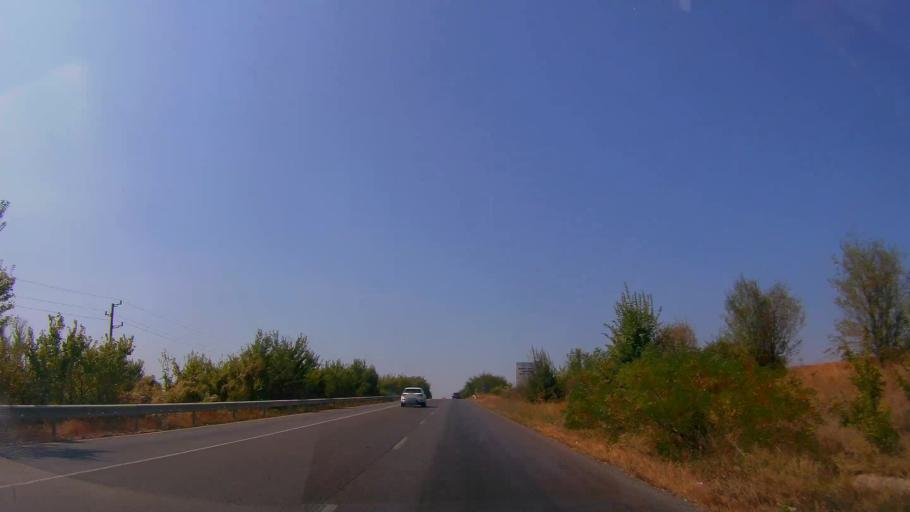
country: BG
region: Ruse
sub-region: Obshtina Vetovo
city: Senovo
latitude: 43.5615
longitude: 26.3654
